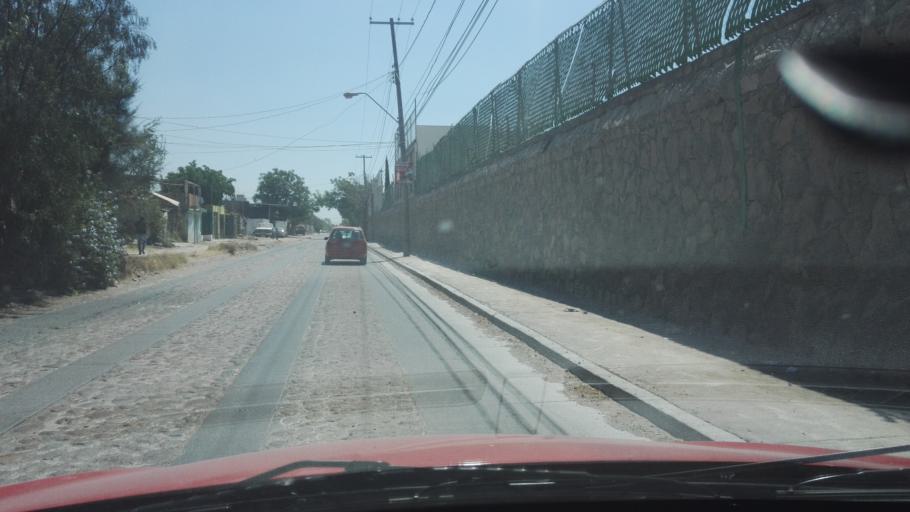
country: MX
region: Guanajuato
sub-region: Leon
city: Fraccionamiento Paraiso Real
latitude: 21.0944
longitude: -101.6003
